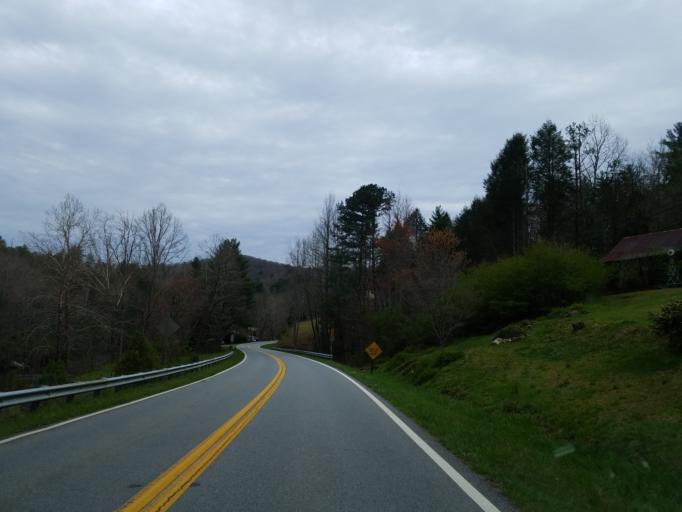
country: US
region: Georgia
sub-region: Fannin County
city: Blue Ridge
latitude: 34.7968
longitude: -84.2784
